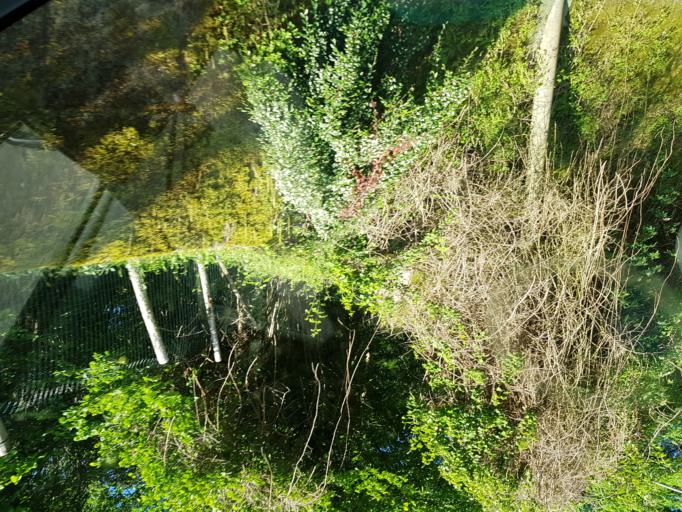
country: IT
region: Liguria
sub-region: Provincia di Genova
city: Manesseno
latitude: 44.4715
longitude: 8.9174
